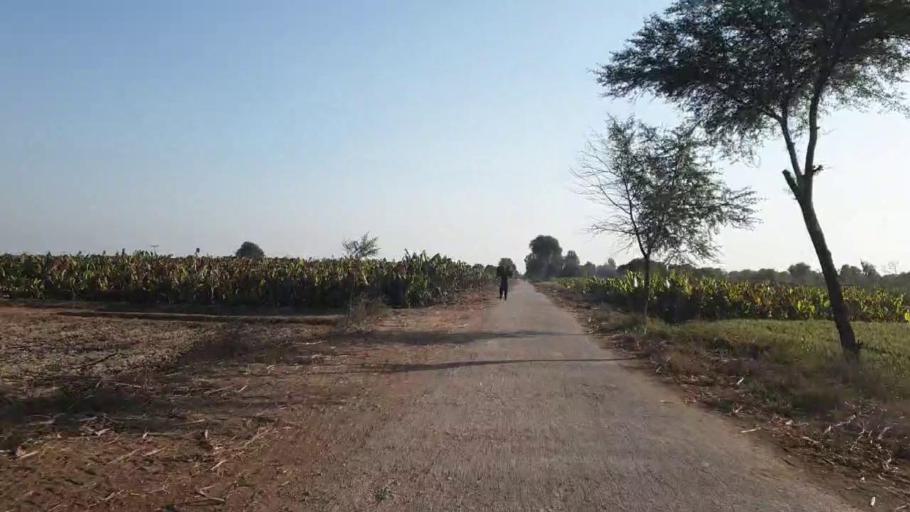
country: PK
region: Sindh
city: Tando Allahyar
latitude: 25.3709
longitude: 68.6825
